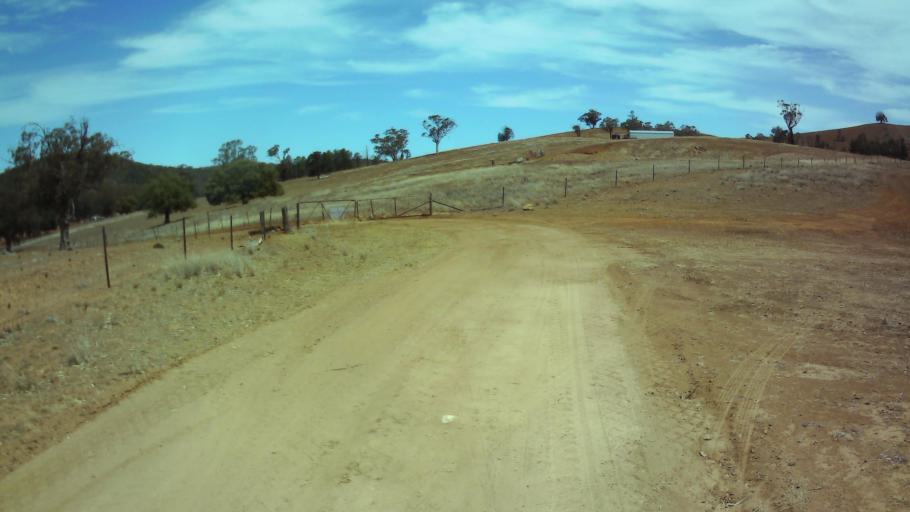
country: AU
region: New South Wales
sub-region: Weddin
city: Grenfell
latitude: -33.7890
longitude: 148.1568
